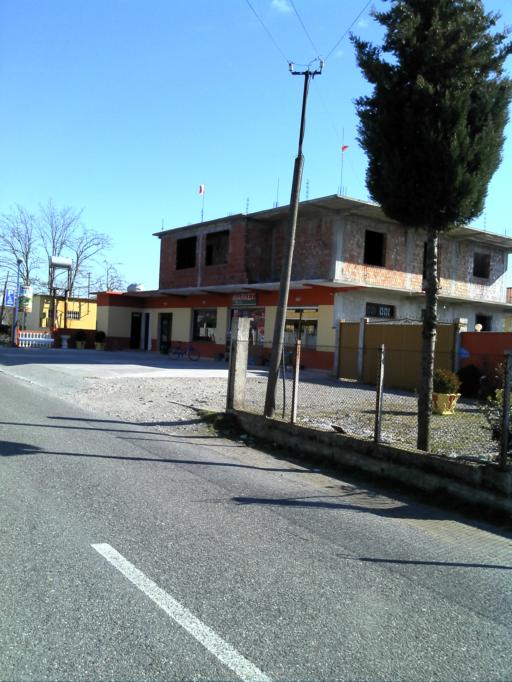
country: AL
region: Shkoder
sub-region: Rrethi i Shkodres
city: Dajc
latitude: 42.0154
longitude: 19.4343
